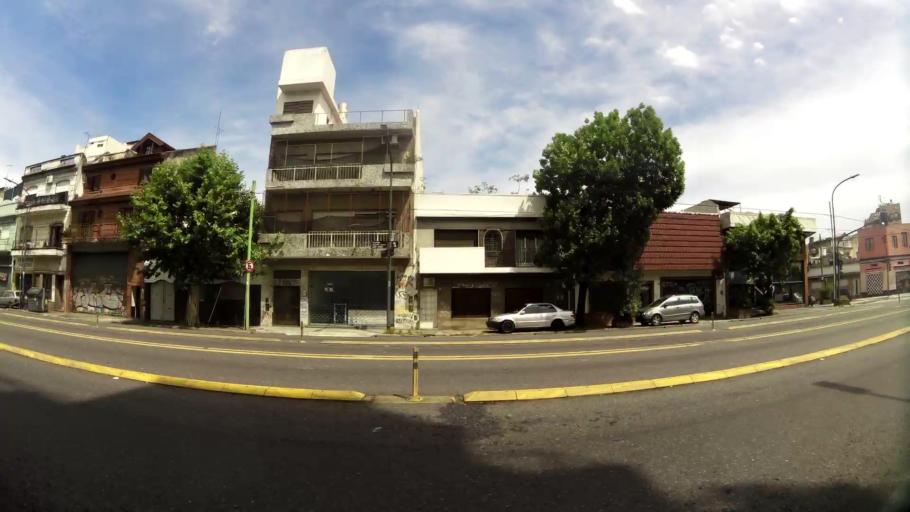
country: AR
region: Buenos Aires F.D.
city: Villa Santa Rita
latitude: -34.6260
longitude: -58.4881
